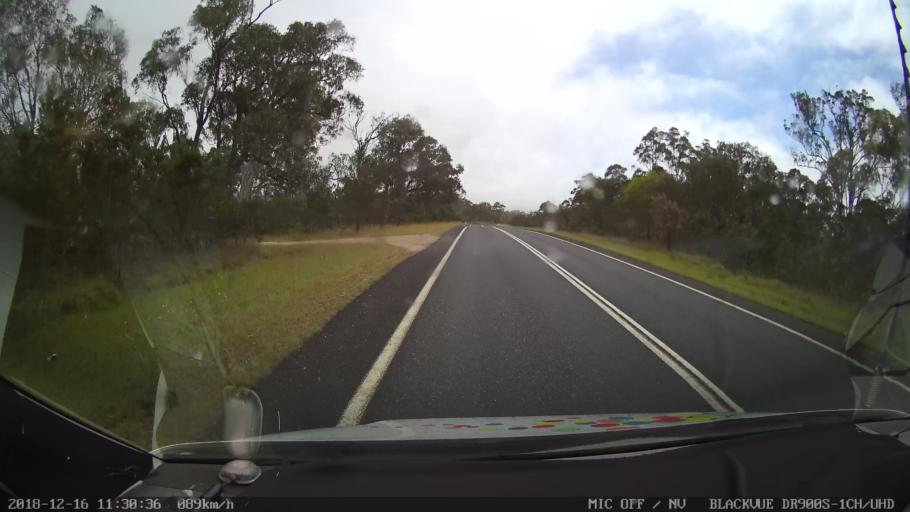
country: AU
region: New South Wales
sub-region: Tenterfield Municipality
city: Carrolls Creek
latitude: -29.0305
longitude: 152.1213
